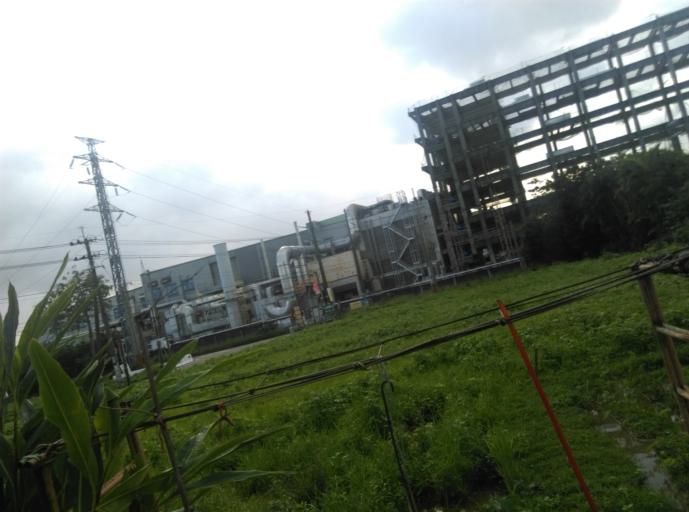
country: TW
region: Taiwan
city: Taoyuan City
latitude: 24.9925
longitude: 121.2528
